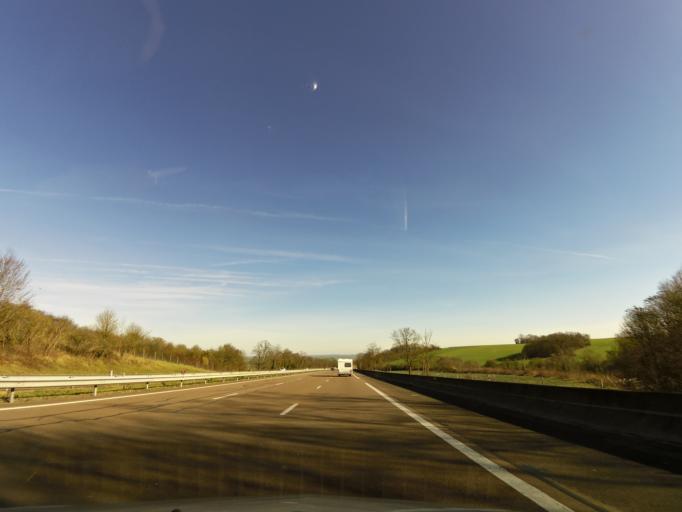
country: FR
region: Bourgogne
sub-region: Departement de l'Yonne
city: Aillant-sur-Tholon
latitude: 47.9107
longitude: 3.3158
